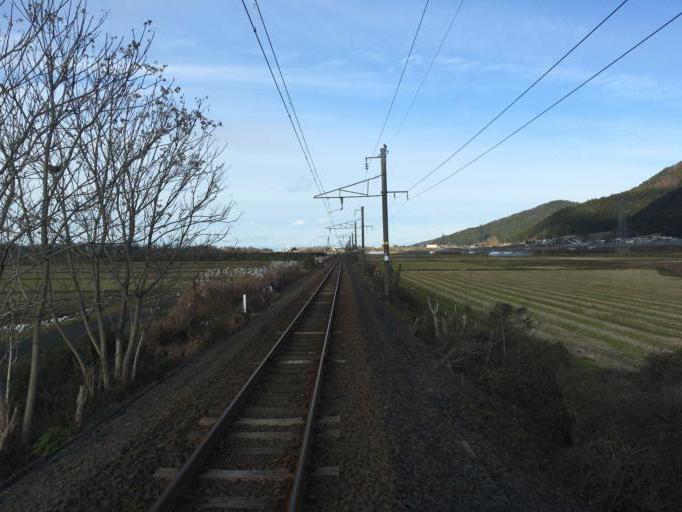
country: JP
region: Akita
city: Yuzawa
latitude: 39.1142
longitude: 140.4841
